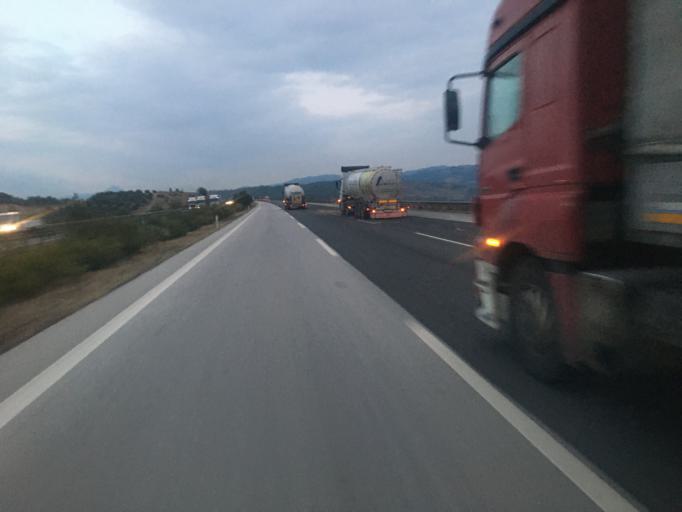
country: TR
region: Osmaniye
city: Kaypak
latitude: 37.1558
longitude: 36.3521
